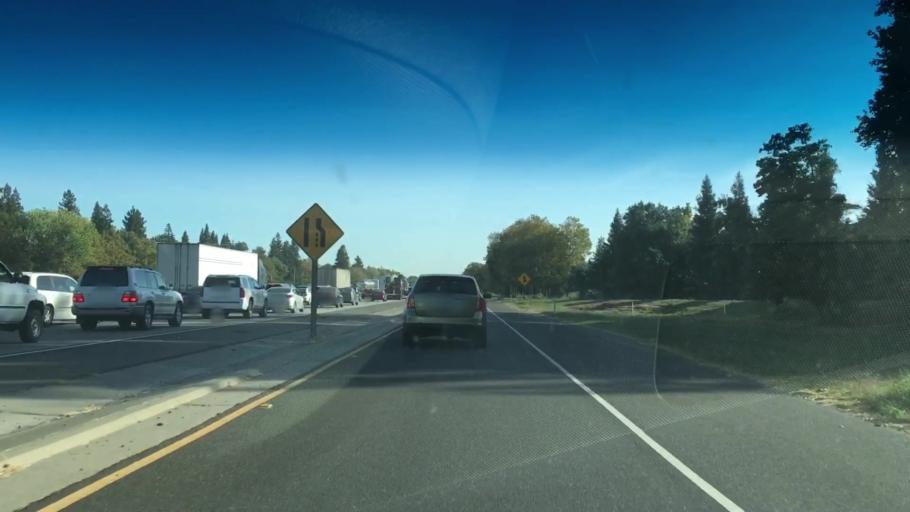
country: US
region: California
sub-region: Sacramento County
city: Parkway
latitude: 38.4948
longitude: -121.5166
